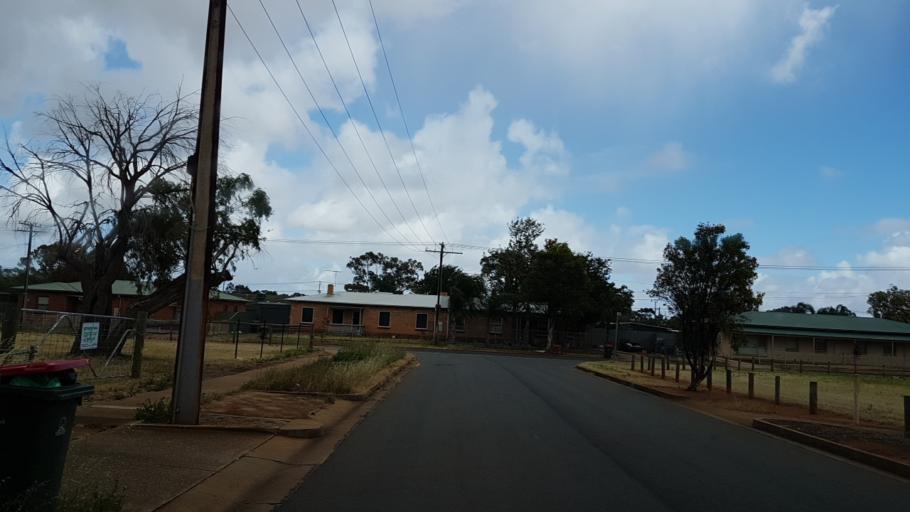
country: AU
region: South Australia
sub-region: Playford
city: Smithfield
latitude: -34.6939
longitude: 138.6644
